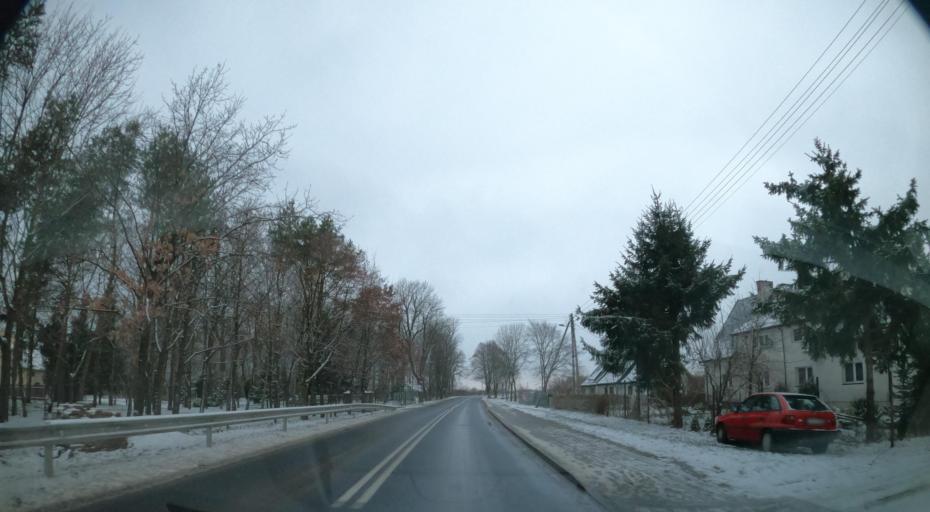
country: PL
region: Masovian Voivodeship
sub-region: Powiat plocki
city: Nowy Duninow
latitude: 52.6141
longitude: 19.4609
